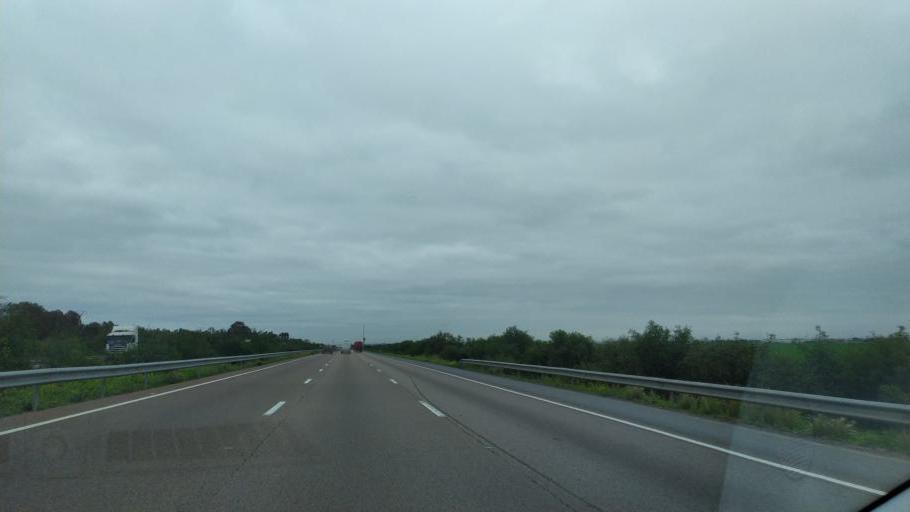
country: MA
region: Chaouia-Ouardigha
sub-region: Benslimane
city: Bouznika
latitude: 33.7864
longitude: -7.2144
